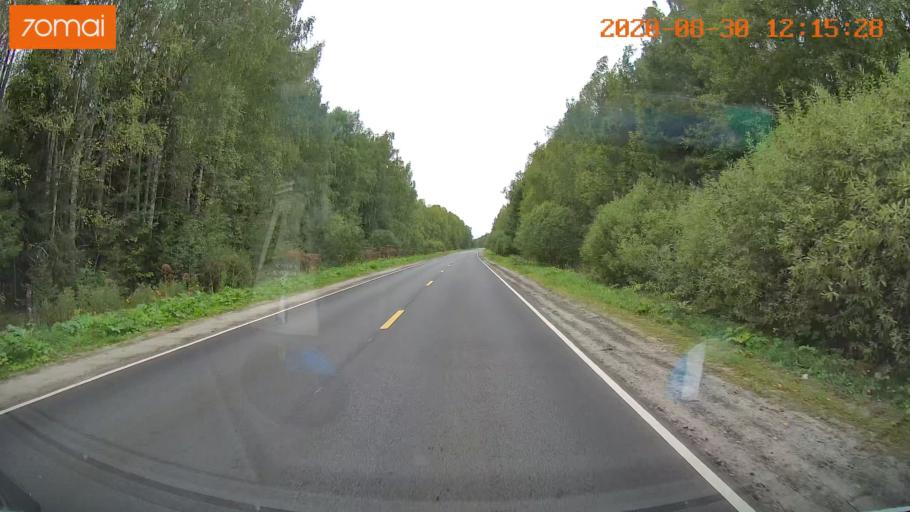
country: RU
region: Ivanovo
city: Yur'yevets
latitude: 57.3174
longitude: 43.0289
